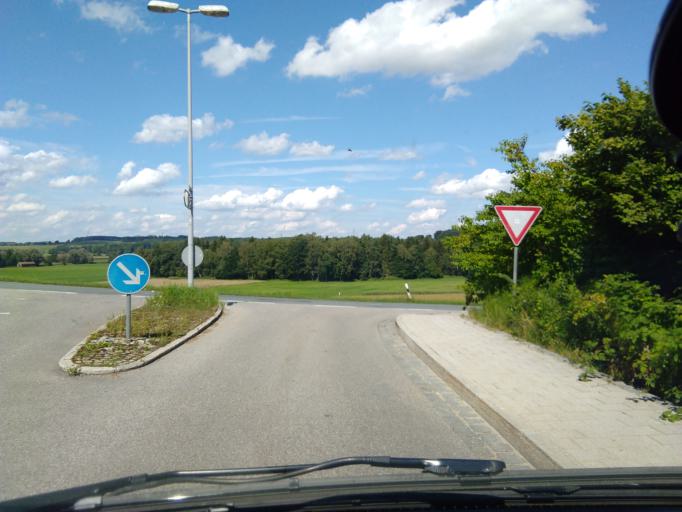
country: DE
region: Bavaria
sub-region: Upper Bavaria
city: Assling
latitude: 47.9932
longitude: 11.9932
